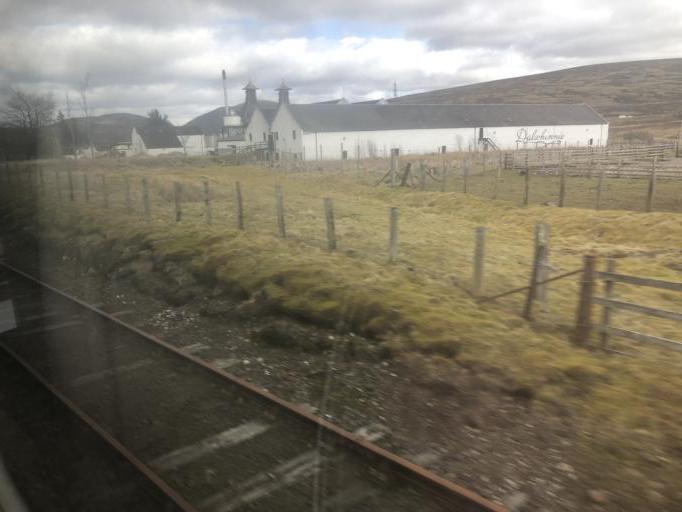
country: GB
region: Scotland
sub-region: Highland
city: Kingussie
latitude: 56.9397
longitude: -4.2419
